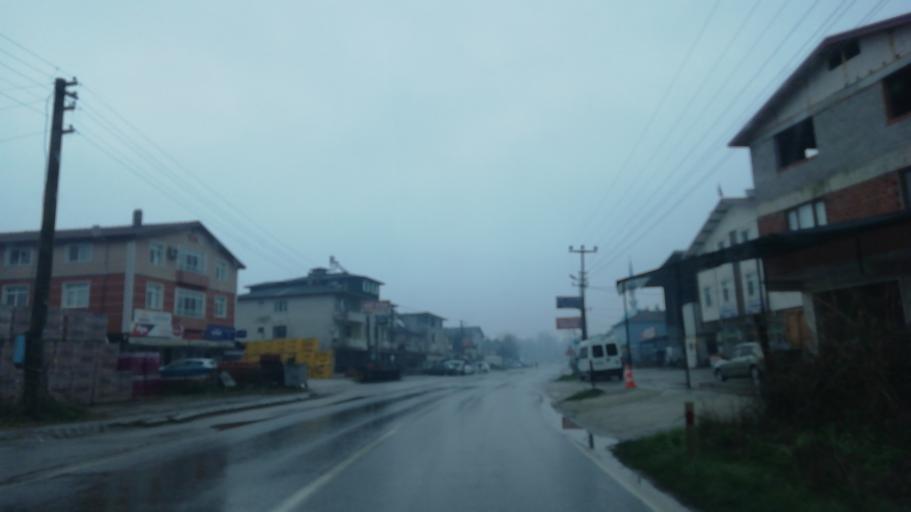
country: TR
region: Sakarya
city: Karapurcek
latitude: 40.6899
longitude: 30.4887
